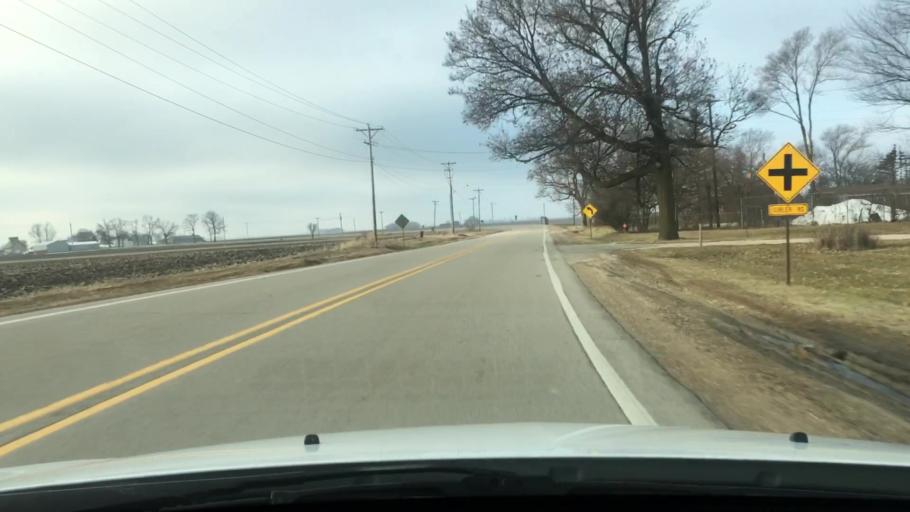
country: US
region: Illinois
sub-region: Ogle County
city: Rochelle
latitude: 41.8923
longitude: -89.0697
